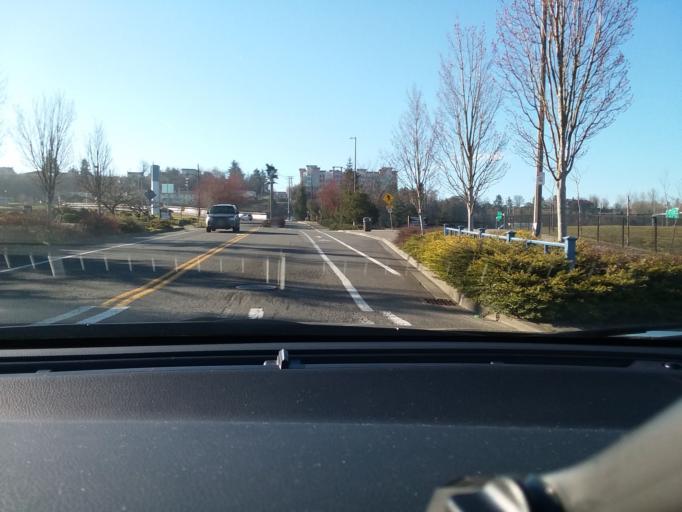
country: US
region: Washington
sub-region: Pierce County
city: Tacoma
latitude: 47.2363
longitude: -122.4286
